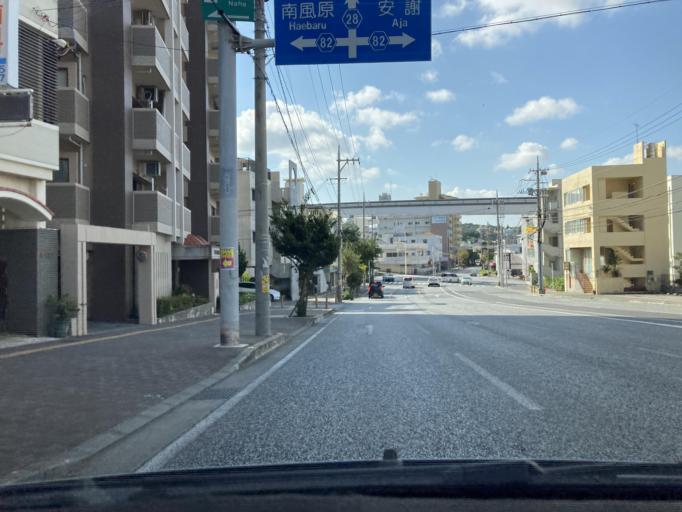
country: JP
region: Okinawa
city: Naha-shi
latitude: 26.2261
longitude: 127.7184
